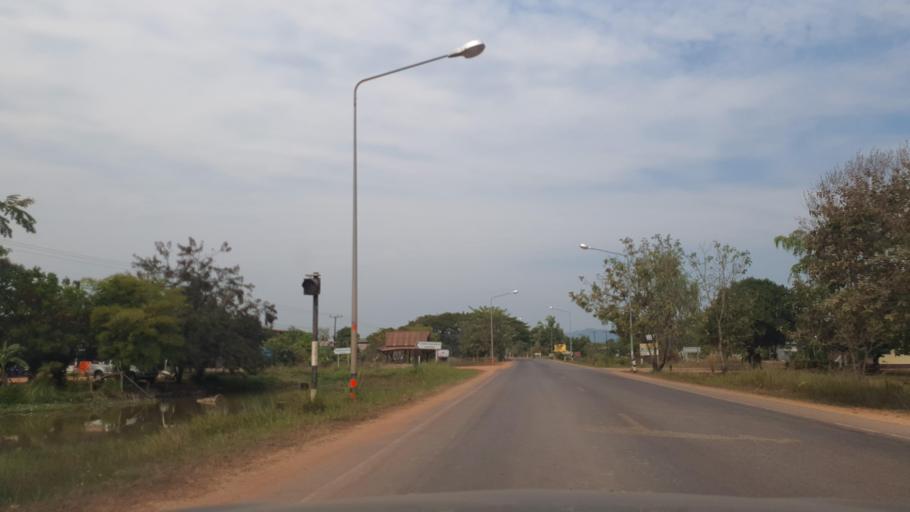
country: TH
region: Changwat Bueng Kan
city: Bung Khla
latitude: 18.1995
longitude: 104.0521
